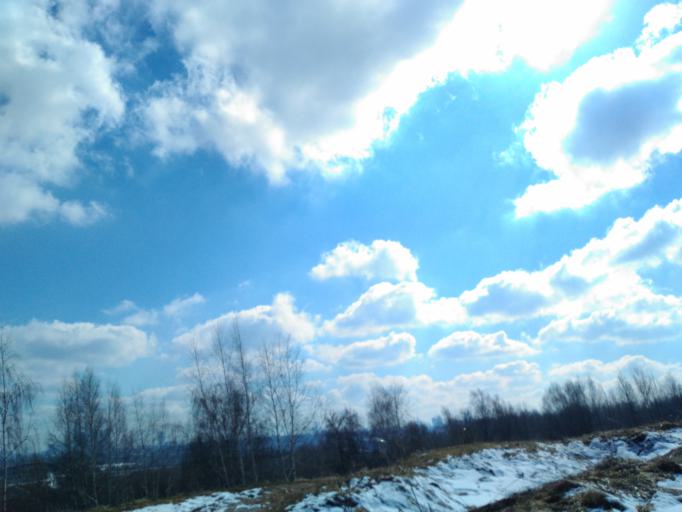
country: RU
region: Moscow
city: Shchukino
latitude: 55.7675
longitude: 37.4233
